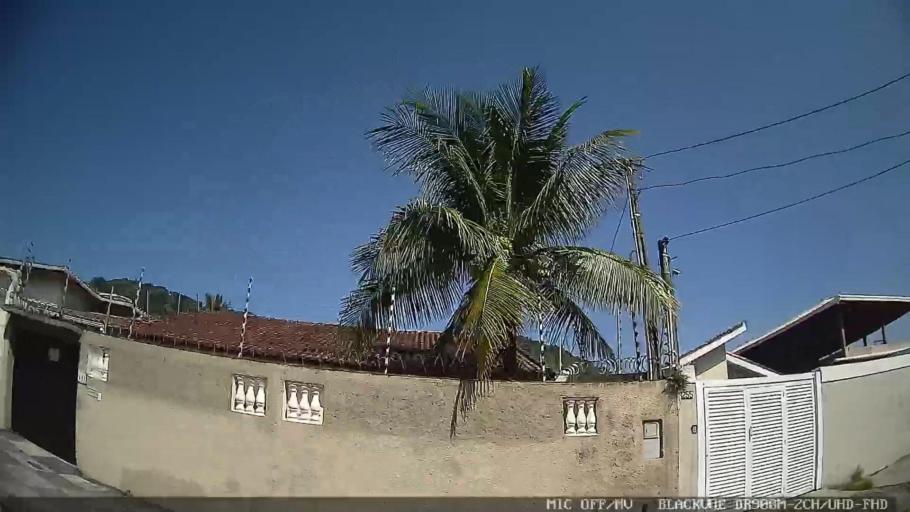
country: BR
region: Sao Paulo
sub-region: Guaruja
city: Guaruja
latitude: -24.0138
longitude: -46.2783
